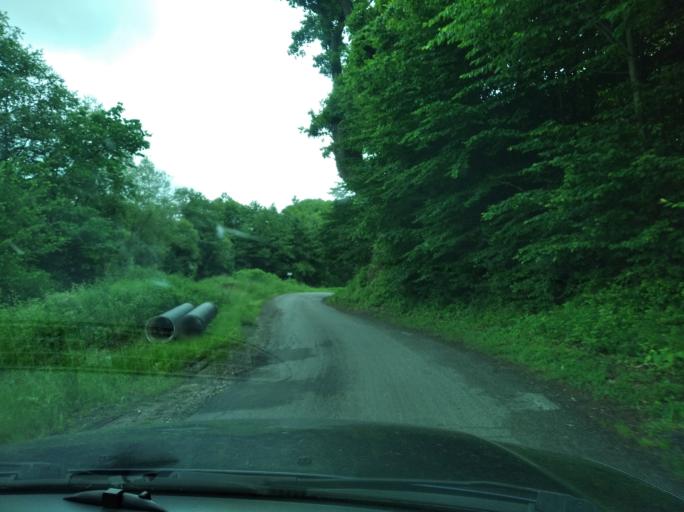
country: PL
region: Subcarpathian Voivodeship
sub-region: Powiat przemyski
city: Nienadowa
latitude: 49.8511
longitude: 22.4113
